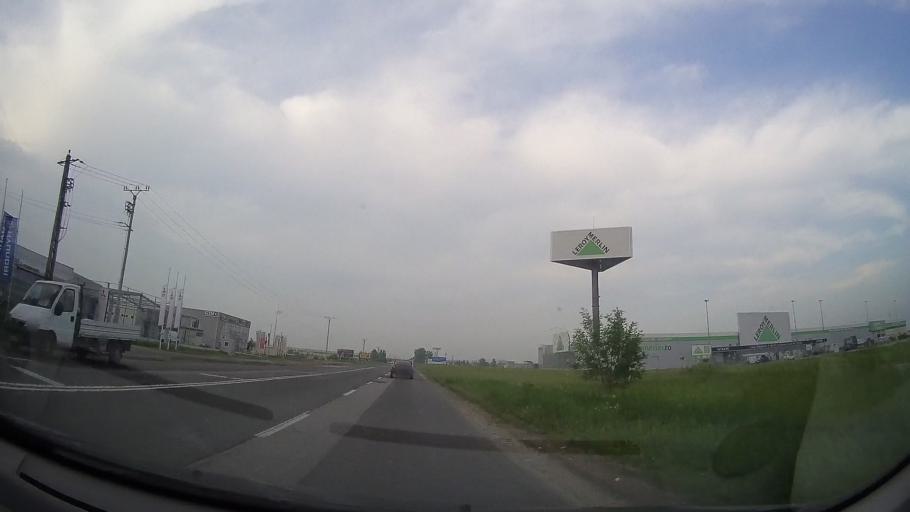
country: RO
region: Timis
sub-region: Comuna Giroc
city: Chisoda
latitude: 45.7044
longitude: 21.1852
